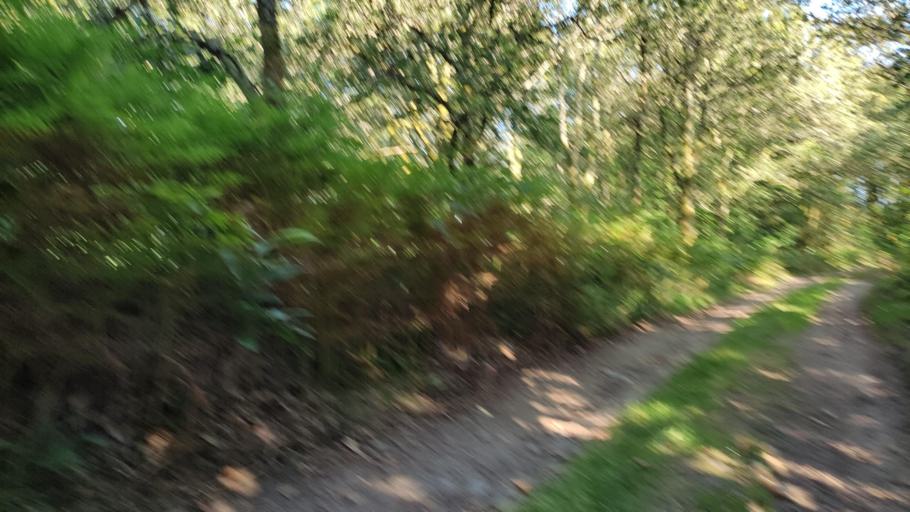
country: FR
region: Limousin
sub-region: Departement de la Haute-Vienne
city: Ambazac
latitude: 46.0362
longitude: 1.4613
